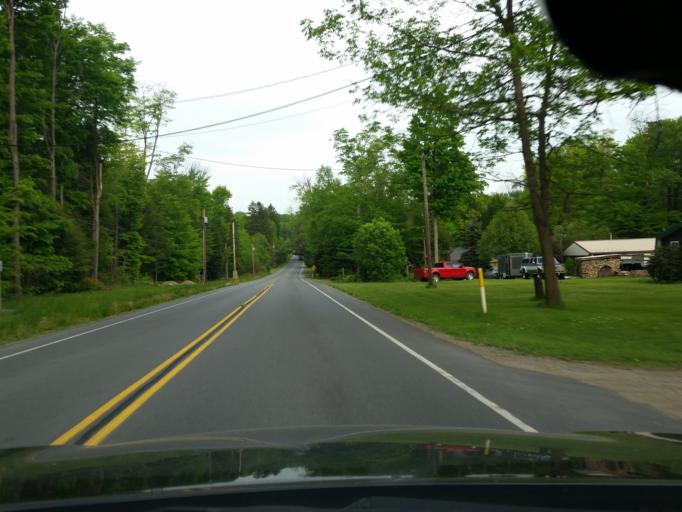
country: US
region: Pennsylvania
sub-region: McKean County
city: Kane
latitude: 41.5733
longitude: -78.9140
